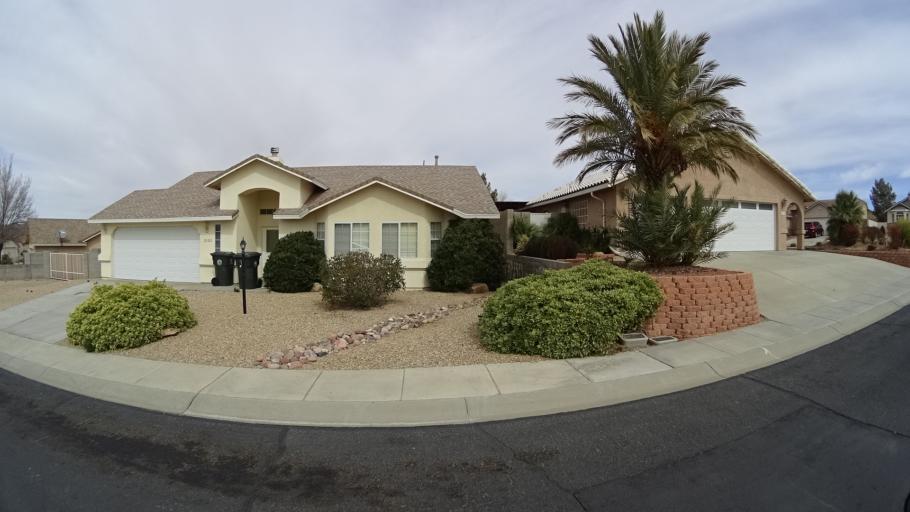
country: US
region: Arizona
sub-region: Mohave County
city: Kingman
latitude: 35.1847
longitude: -114.0094
